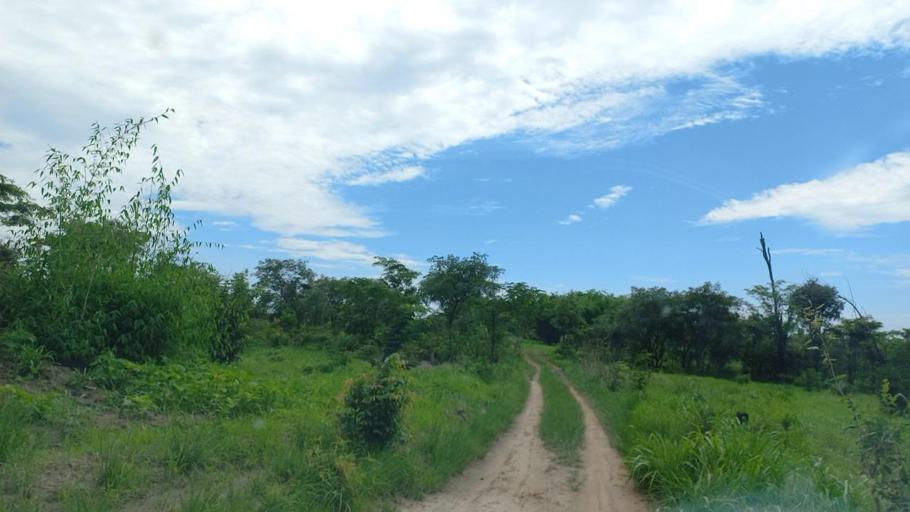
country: ZM
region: Copperbelt
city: Kitwe
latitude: -12.7897
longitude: 28.3977
